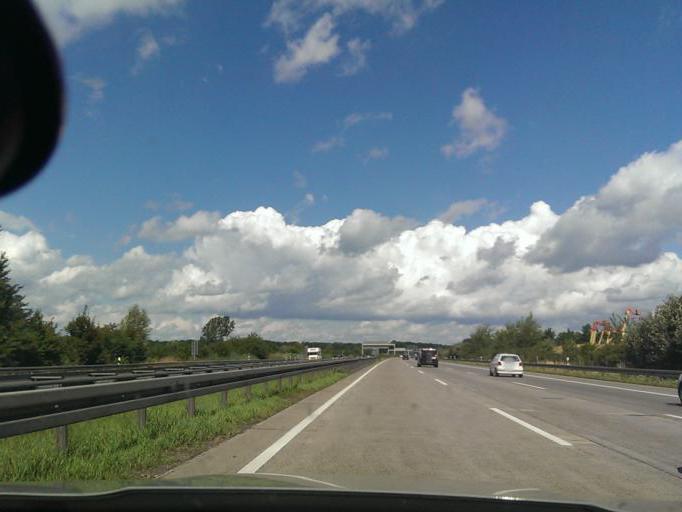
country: DE
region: Lower Saxony
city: Isernhagen Farster Bauerschaft
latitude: 52.4413
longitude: 9.8716
